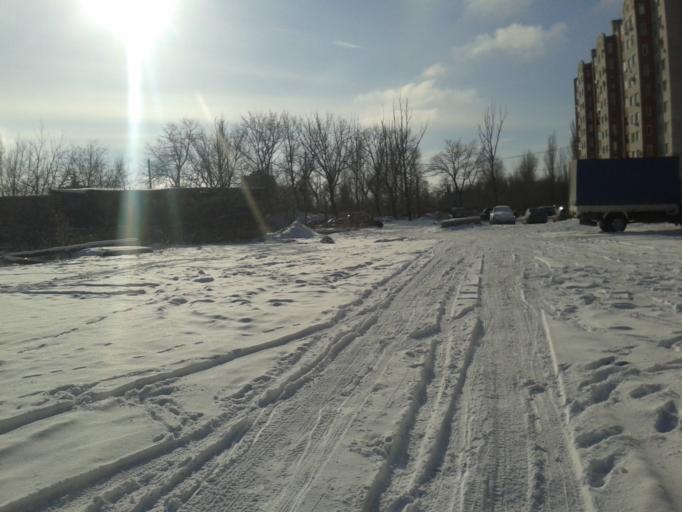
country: RU
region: Volgograd
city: Volgograd
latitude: 48.7445
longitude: 44.4949
